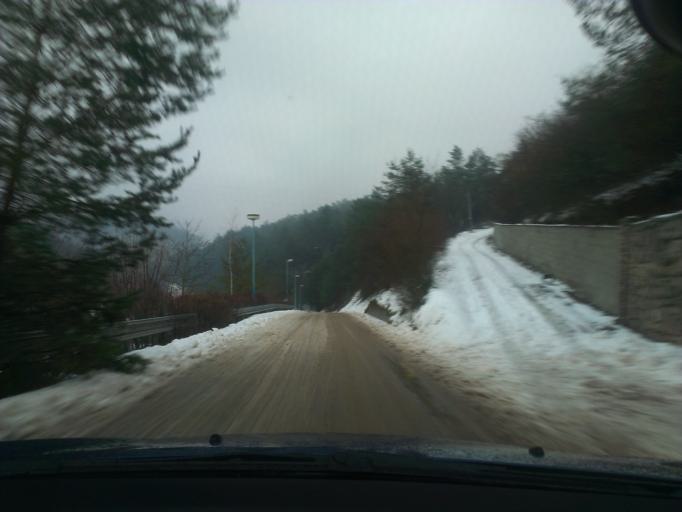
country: SK
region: Trnavsky
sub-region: Okres Trnava
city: Piestany
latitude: 48.5780
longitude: 17.8558
